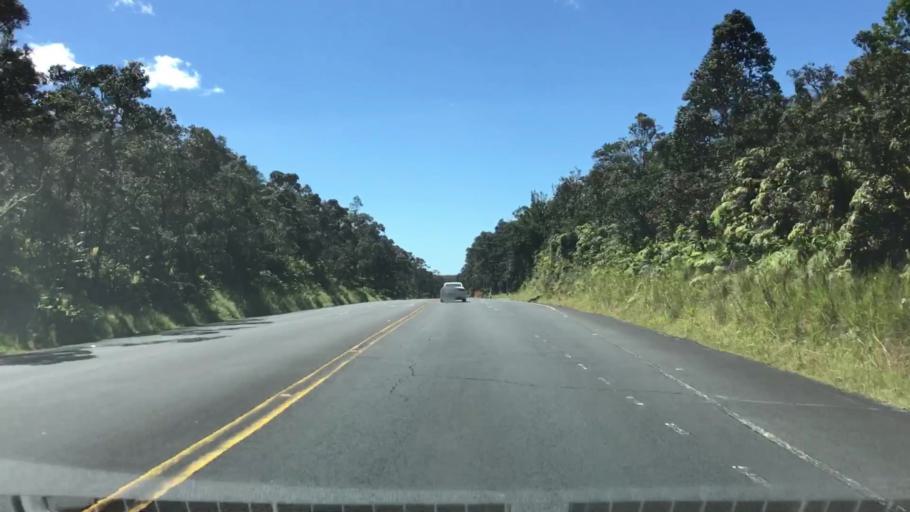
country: US
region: Hawaii
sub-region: Hawaii County
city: Volcano
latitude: 19.4301
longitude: -155.2538
